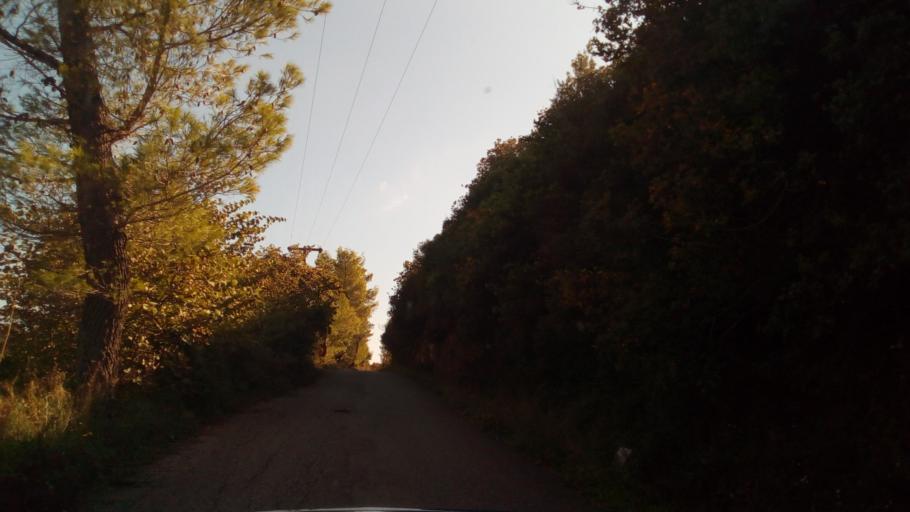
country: GR
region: West Greece
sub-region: Nomos Aitolias kai Akarnanias
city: Nafpaktos
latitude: 38.4192
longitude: 21.8439
